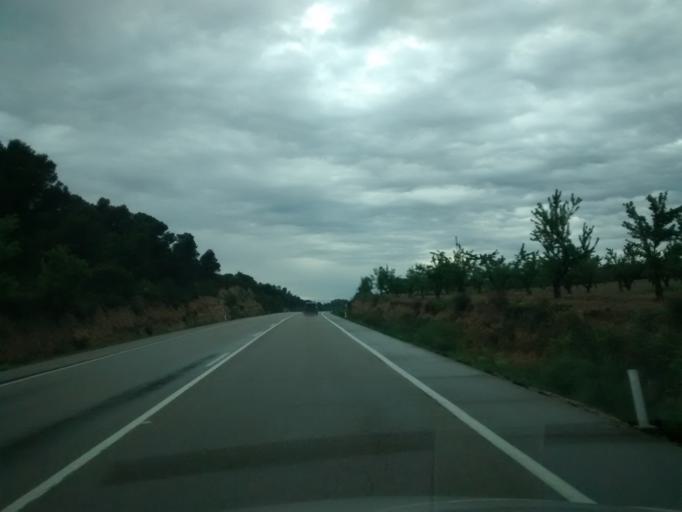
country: ES
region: Aragon
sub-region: Provincia de Zaragoza
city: Maella
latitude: 41.1476
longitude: 0.1081
